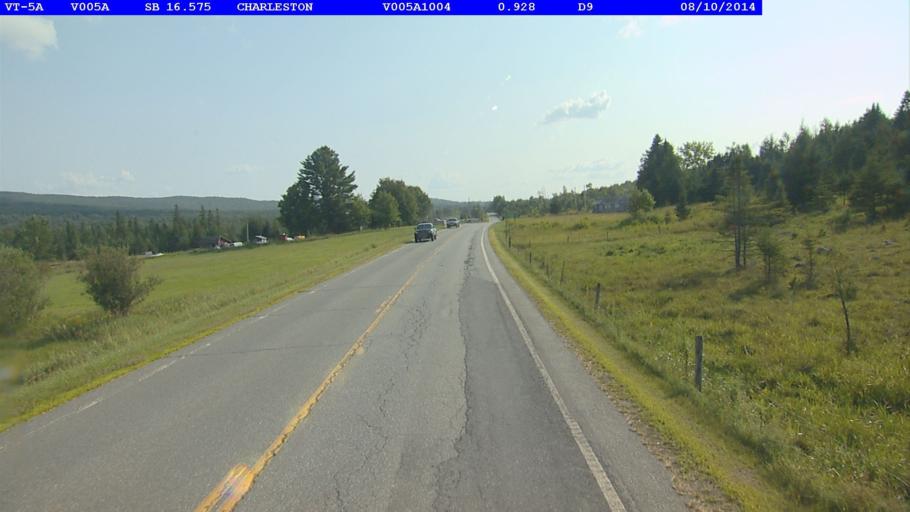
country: US
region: Vermont
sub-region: Orleans County
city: Newport
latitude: 44.8470
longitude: -72.0576
